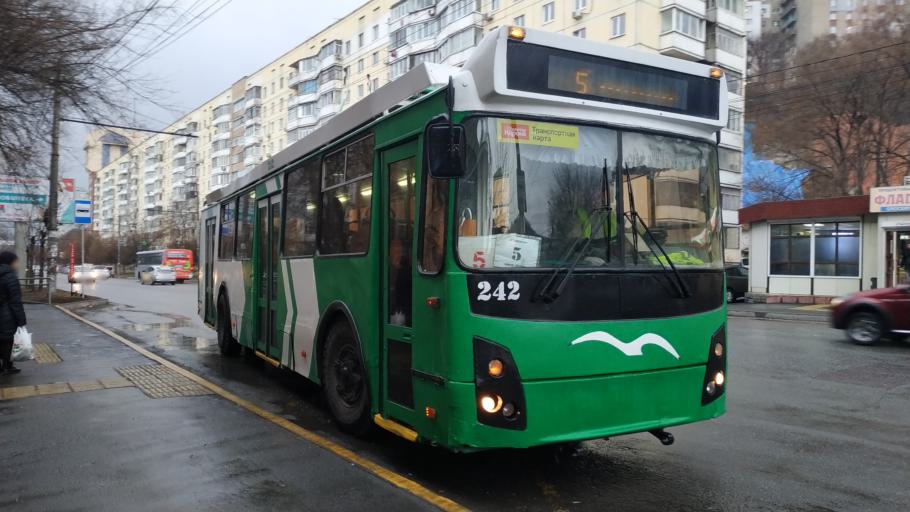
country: RU
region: Primorskiy
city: Vladivostok
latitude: 43.1689
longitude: 131.9317
